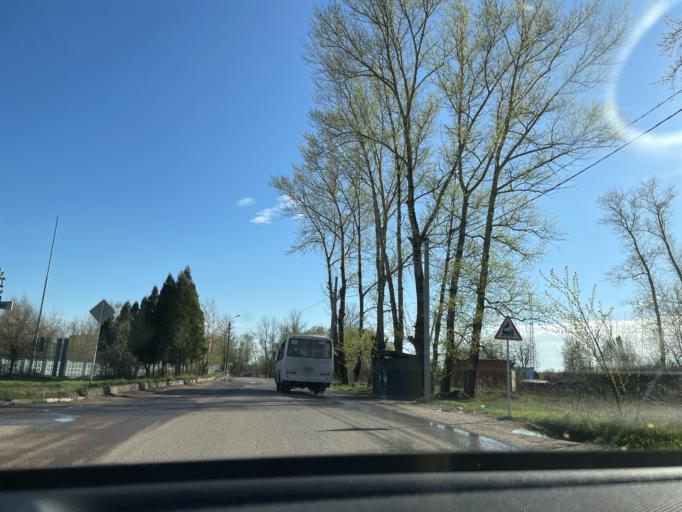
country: RU
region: Tula
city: Aleksin
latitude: 54.4951
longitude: 36.9865
